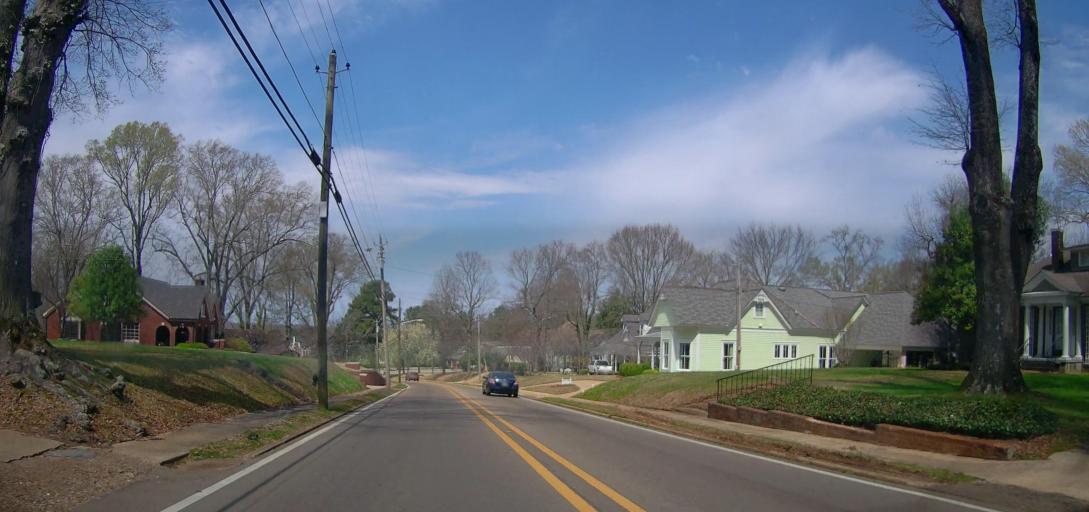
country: US
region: Mississippi
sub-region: Union County
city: New Albany
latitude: 34.4892
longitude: -89.0031
